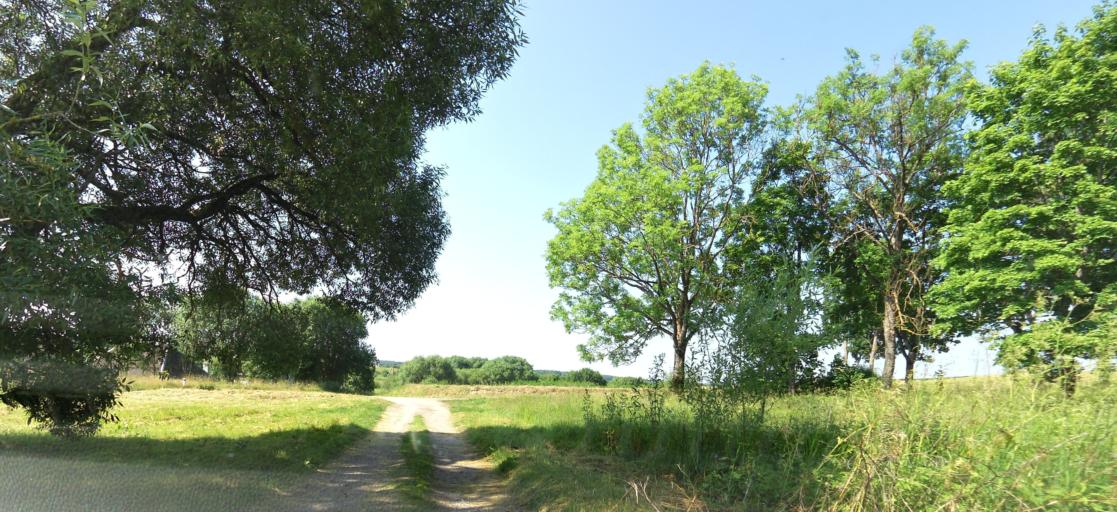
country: LT
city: Grigiskes
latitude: 54.8658
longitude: 25.0614
